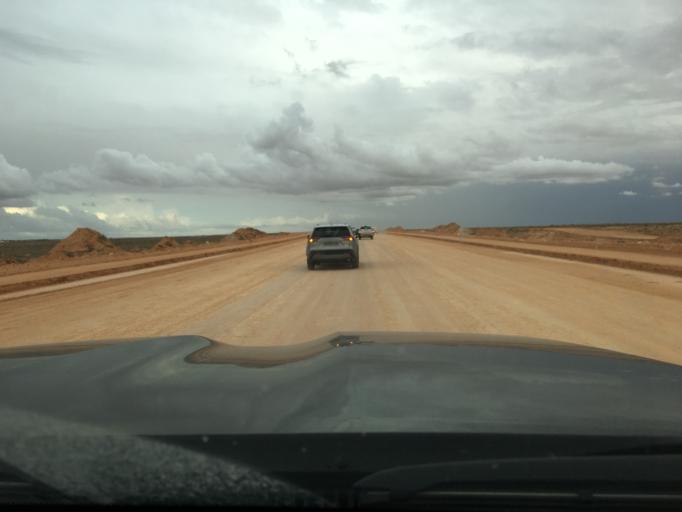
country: TN
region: Madanin
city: Medenine
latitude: 33.2680
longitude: 10.5846
